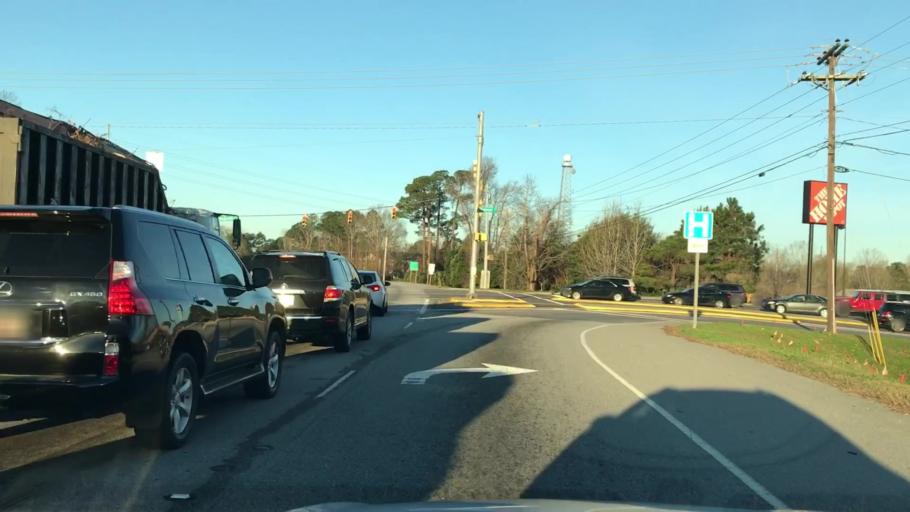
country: US
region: South Carolina
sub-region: Charleston County
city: Shell Point
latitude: 32.8122
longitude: -80.0432
